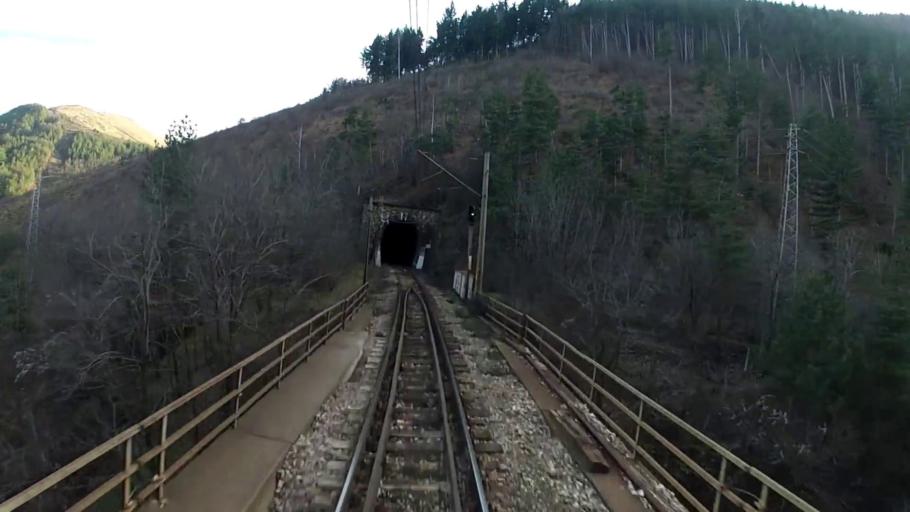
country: BG
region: Plovdiv
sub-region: Obshtina Karlovo
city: Klisura
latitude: 42.6992
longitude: 24.4881
